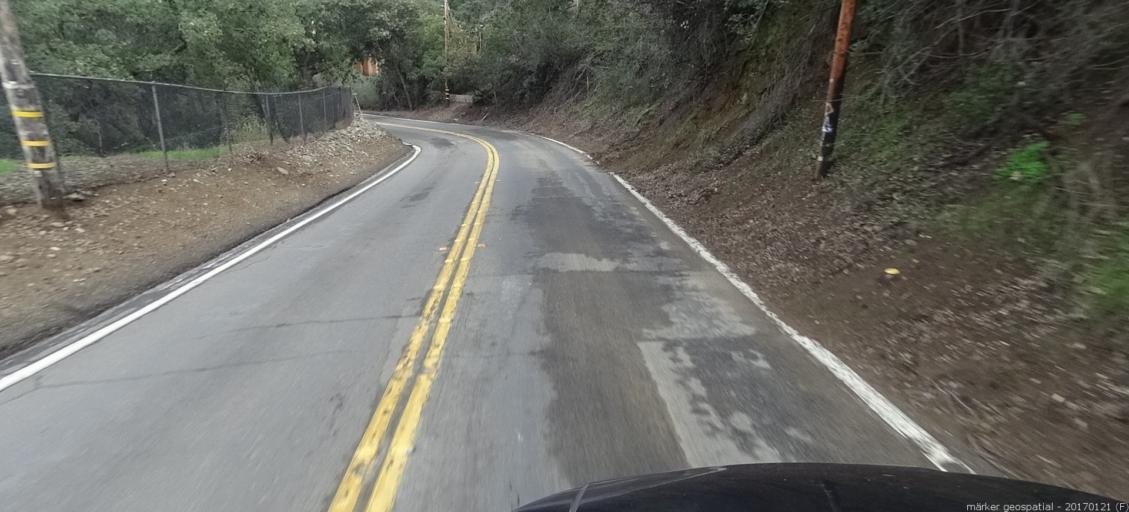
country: US
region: California
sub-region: Orange County
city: Portola Hills
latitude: 33.7074
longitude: -117.6384
